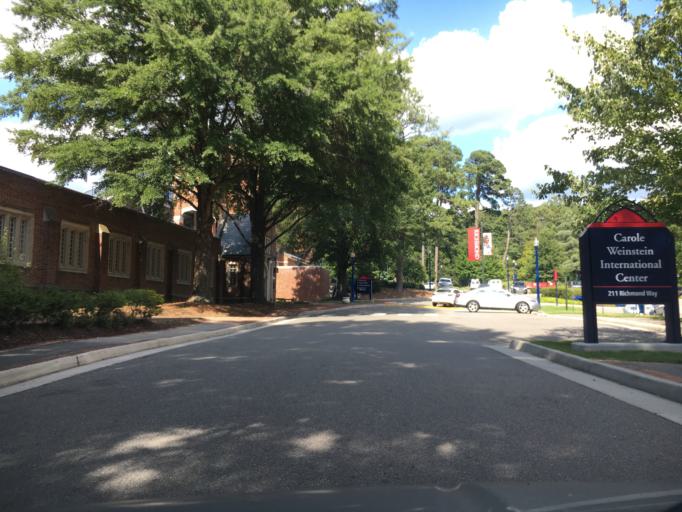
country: US
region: Virginia
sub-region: Henrico County
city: Tuckahoe
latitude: 37.5797
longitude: -77.5371
